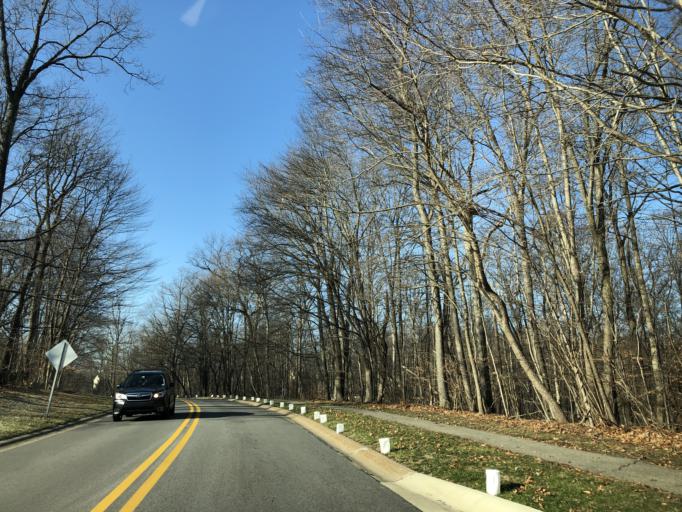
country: US
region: Pennsylvania
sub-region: Chester County
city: Downingtown
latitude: 39.9897
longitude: -75.7030
